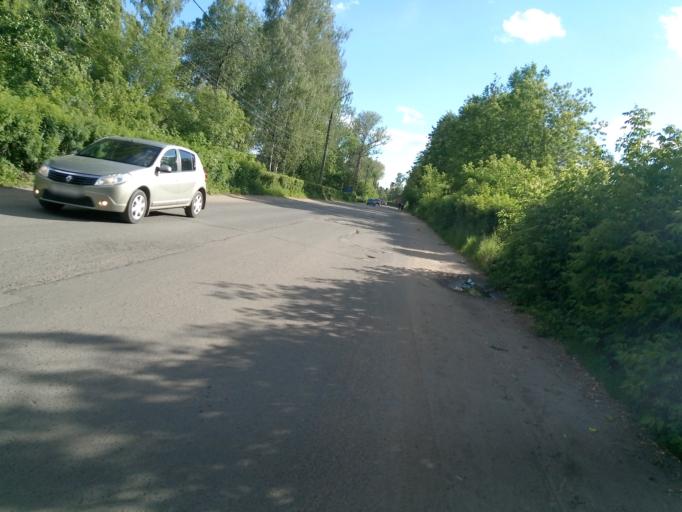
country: RU
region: Jaroslavl
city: Yaroslavl
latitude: 57.6423
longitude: 39.9155
